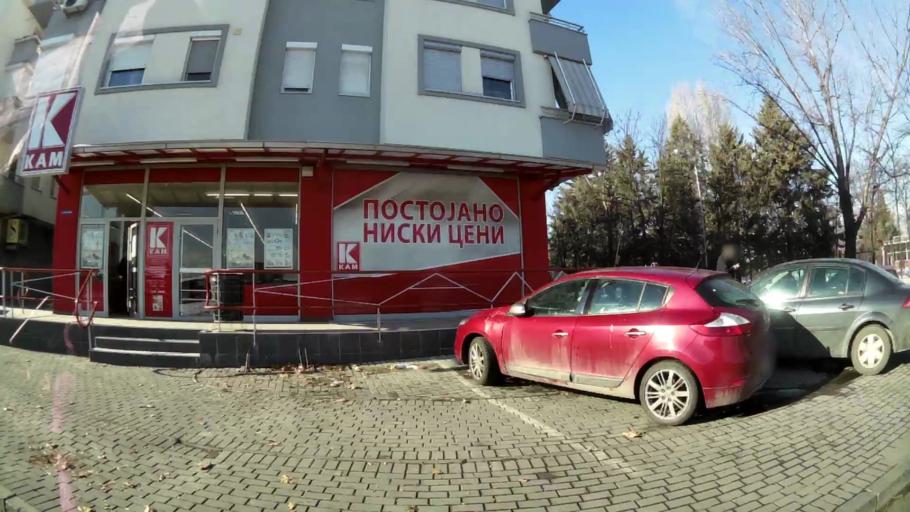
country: MK
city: Krushopek
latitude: 42.0043
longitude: 21.3734
